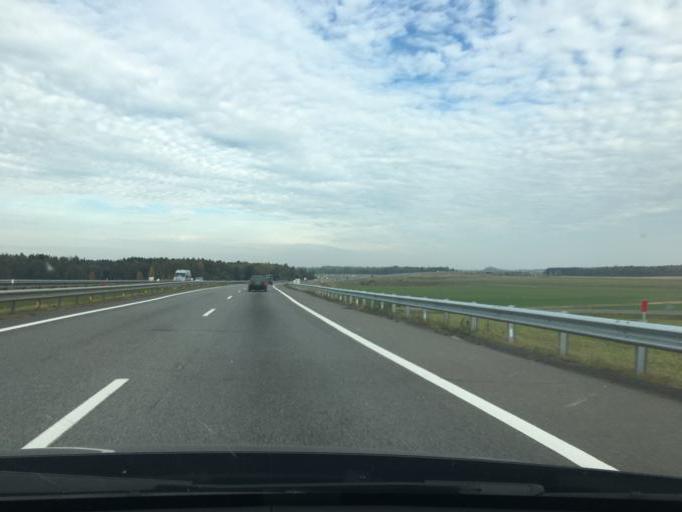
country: BY
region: Minsk
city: Dzyarzhynsk
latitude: 53.6538
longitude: 27.0784
